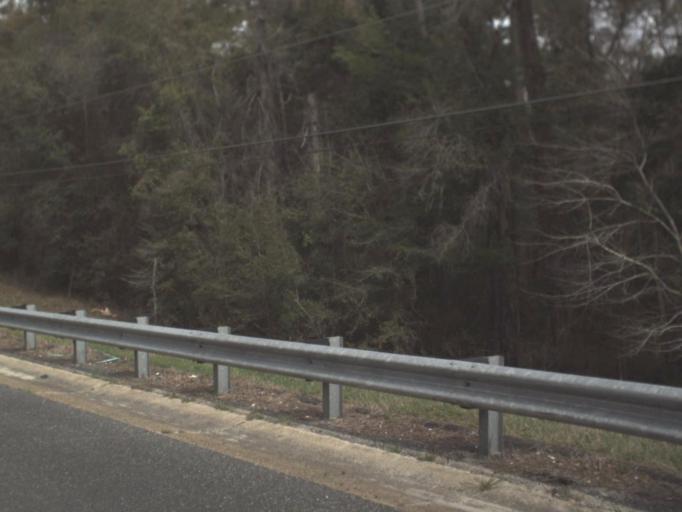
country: US
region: Florida
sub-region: Gadsden County
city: Midway
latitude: 30.4708
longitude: -84.4038
